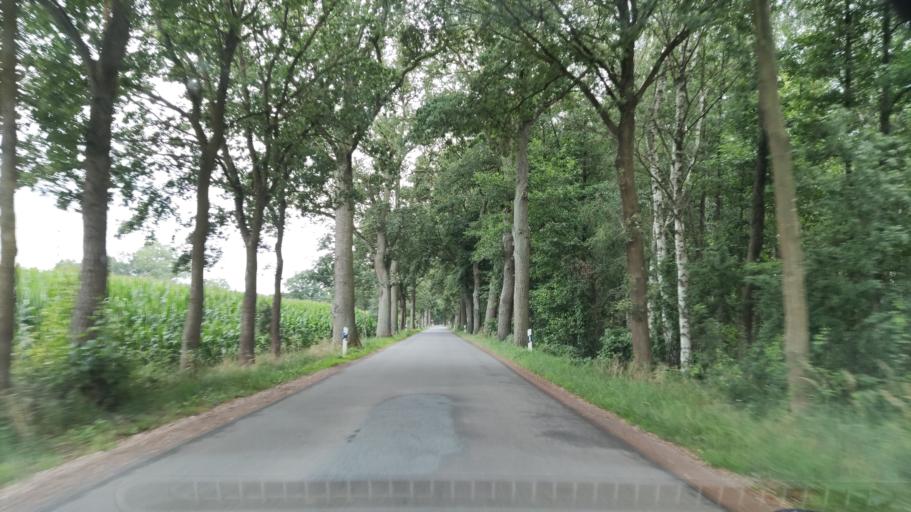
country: DE
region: Lower Saxony
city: Jameln
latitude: 53.0653
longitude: 11.1312
